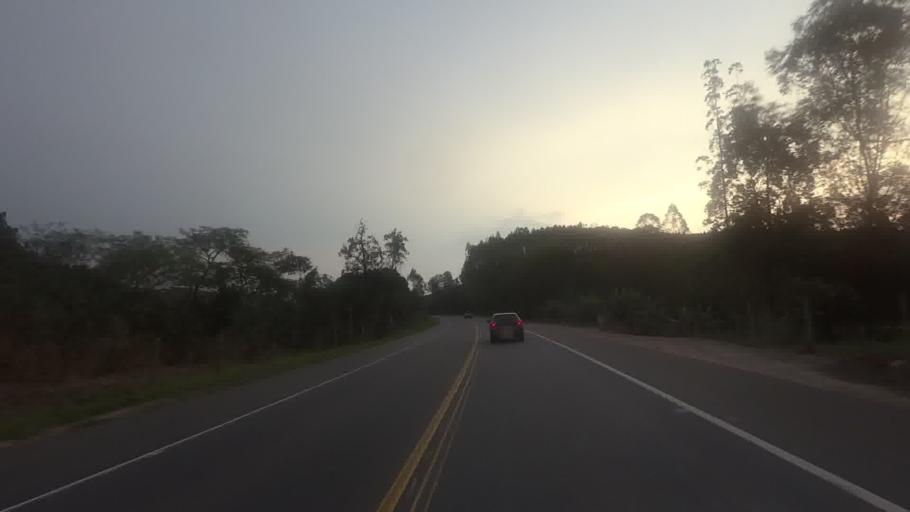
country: BR
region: Rio de Janeiro
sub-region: Carmo
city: Carmo
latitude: -21.7807
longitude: -42.5429
